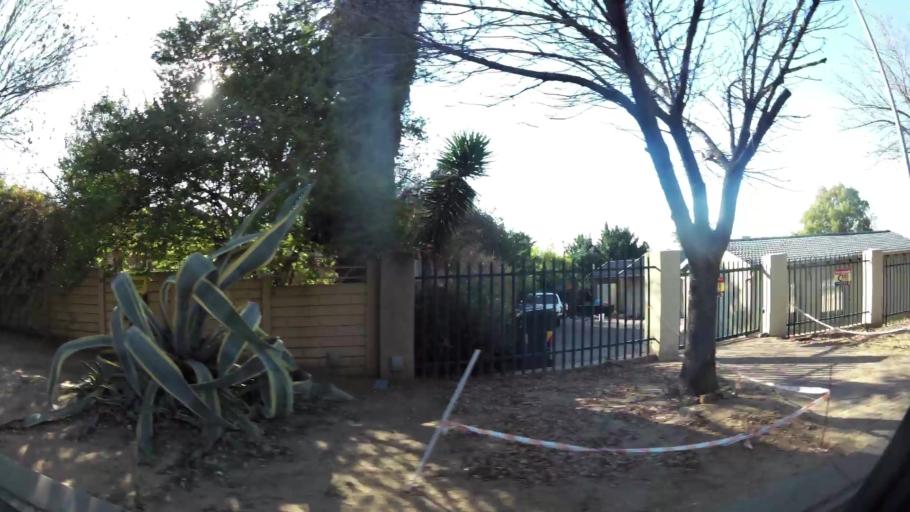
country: ZA
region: Gauteng
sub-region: City of Johannesburg Metropolitan Municipality
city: Roodepoort
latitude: -26.0907
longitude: 27.9626
